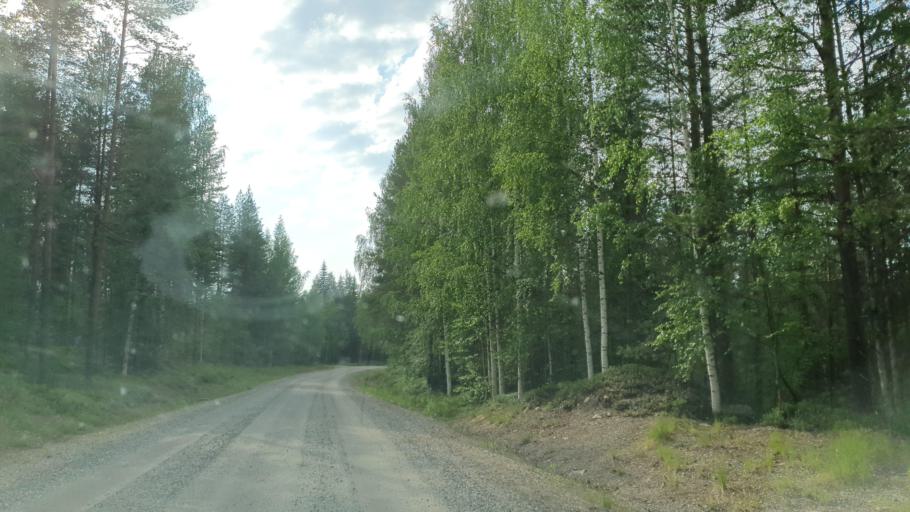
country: FI
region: Kainuu
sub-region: Kehys-Kainuu
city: Kuhmo
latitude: 64.0605
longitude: 29.7626
